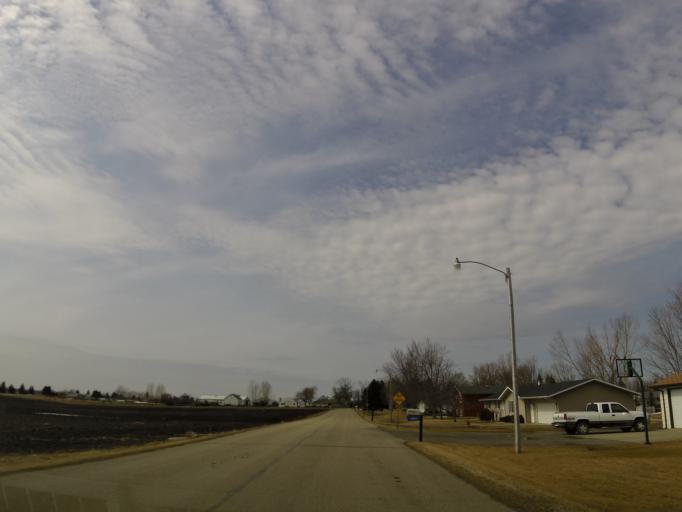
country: US
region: North Dakota
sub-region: Walsh County
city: Grafton
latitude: 48.2915
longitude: -97.3798
